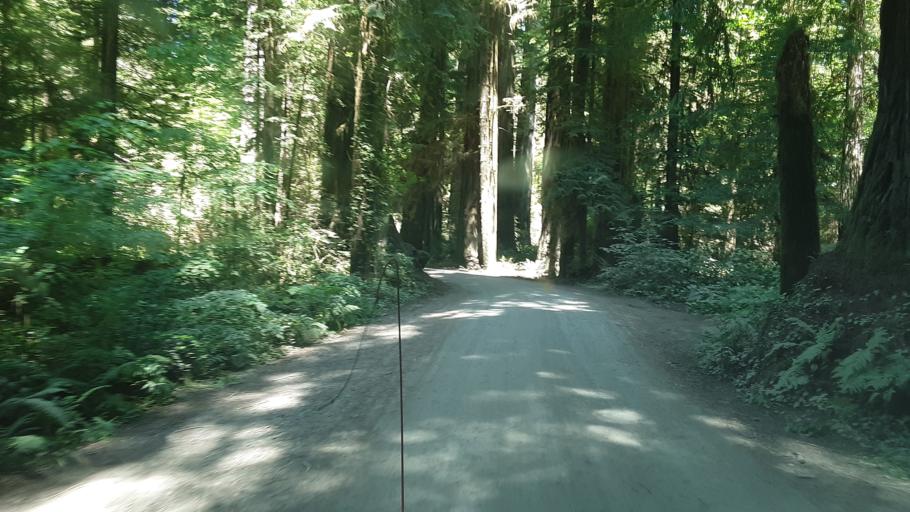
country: US
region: California
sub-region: Del Norte County
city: Bertsch-Oceanview
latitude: 41.8173
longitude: -124.1121
